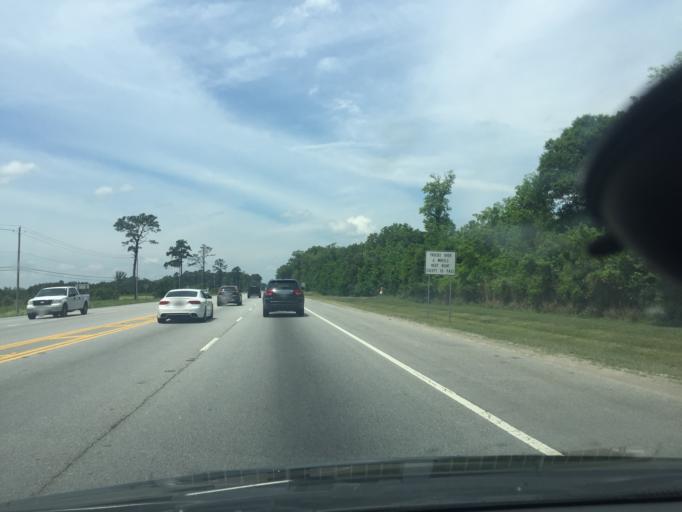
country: US
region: Georgia
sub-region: Chatham County
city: Bloomingdale
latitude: 32.1360
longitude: -81.3103
